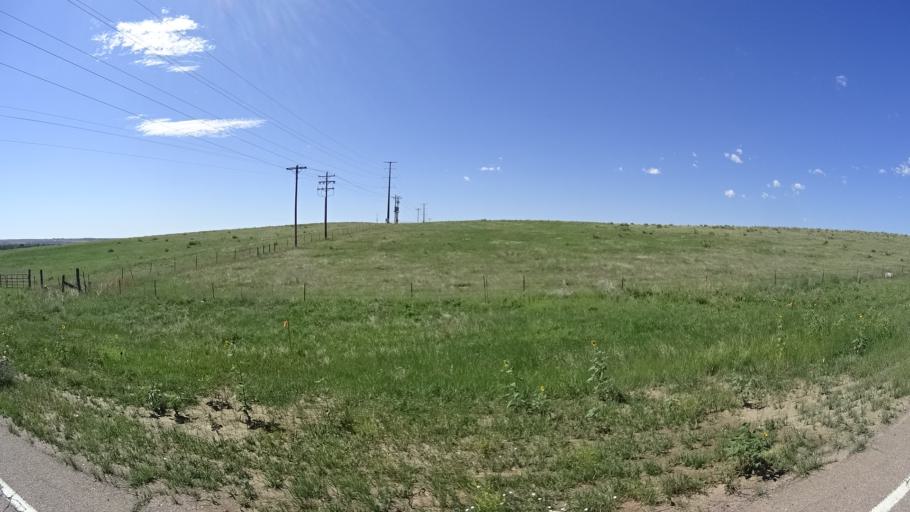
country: US
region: Colorado
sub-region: El Paso County
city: Security-Widefield
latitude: 38.7620
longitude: -104.6740
